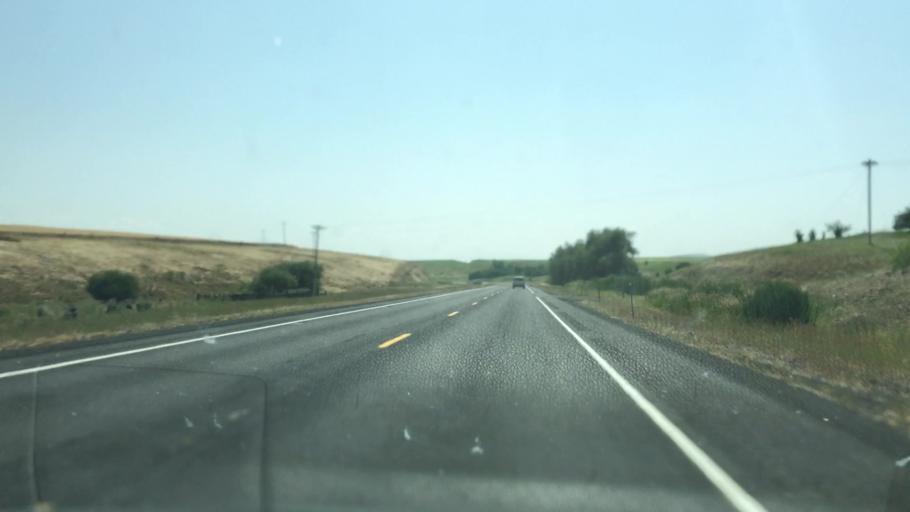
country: US
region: Idaho
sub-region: Lewis County
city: Nezperce
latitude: 46.2245
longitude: -116.4389
